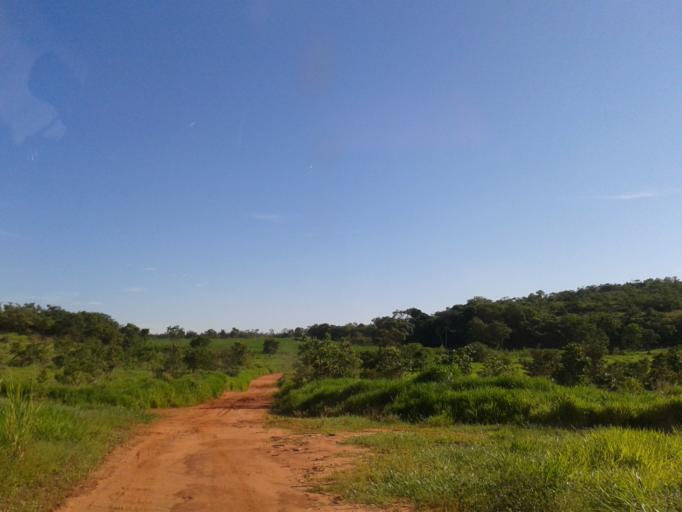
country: BR
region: Minas Gerais
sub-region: Santa Vitoria
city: Santa Vitoria
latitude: -19.1215
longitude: -50.0026
